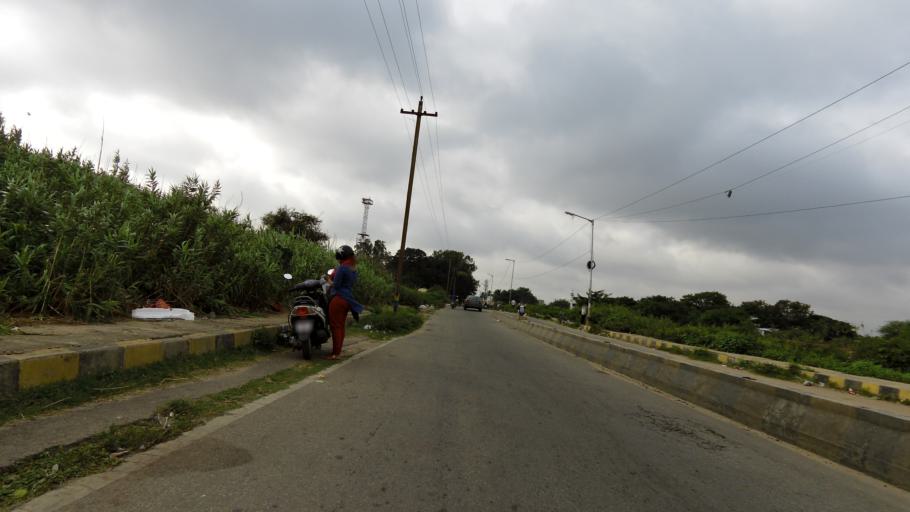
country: IN
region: Karnataka
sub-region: Bangalore Urban
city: Bangalore
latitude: 12.9978
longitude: 77.6414
